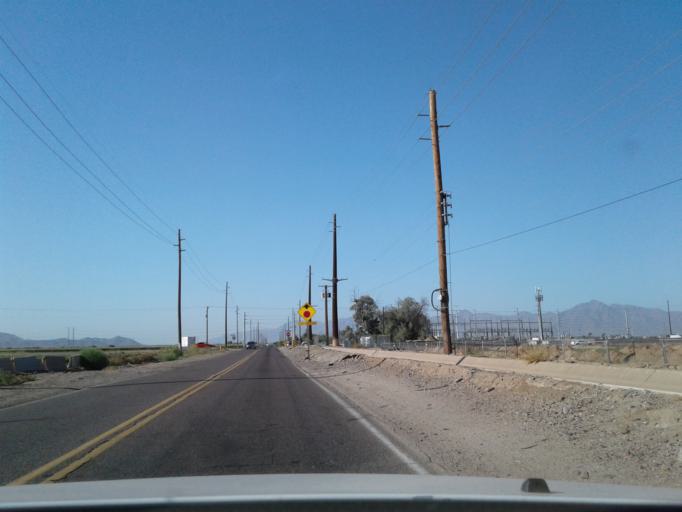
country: US
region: Arizona
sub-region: Maricopa County
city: Laveen
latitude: 33.4238
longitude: -112.1865
